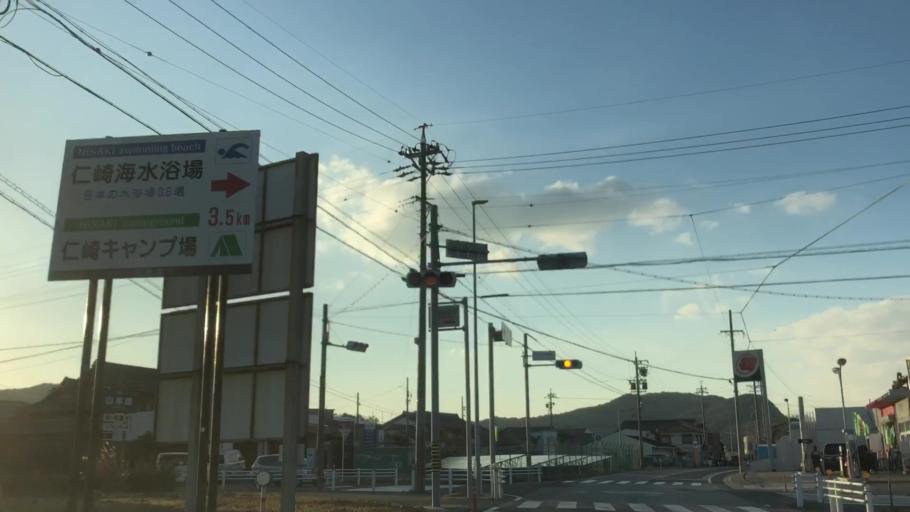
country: JP
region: Aichi
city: Tahara
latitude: 34.6542
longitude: 137.2082
